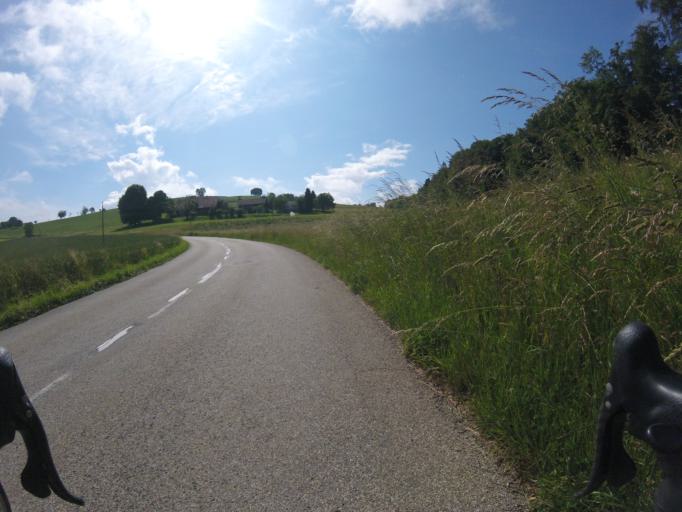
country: CH
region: Bern
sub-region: Bern-Mittelland District
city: Worb
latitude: 46.9388
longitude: 7.5743
